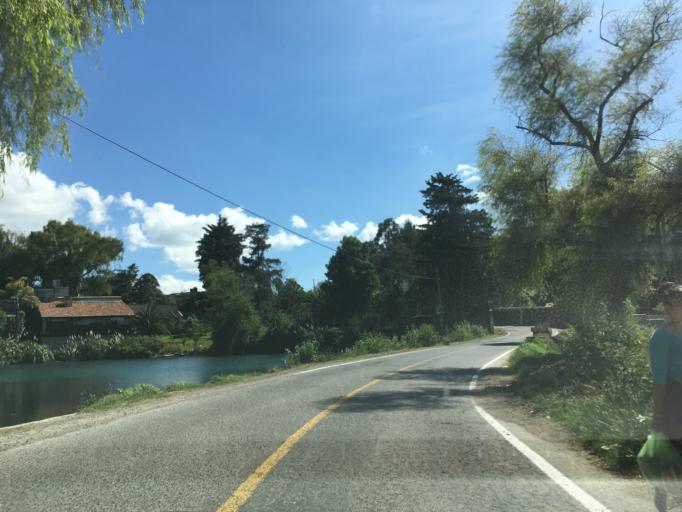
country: MX
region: Hidalgo
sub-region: Omitlan de Juarez
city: San Antonio el Paso
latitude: 20.2221
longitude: -98.5597
